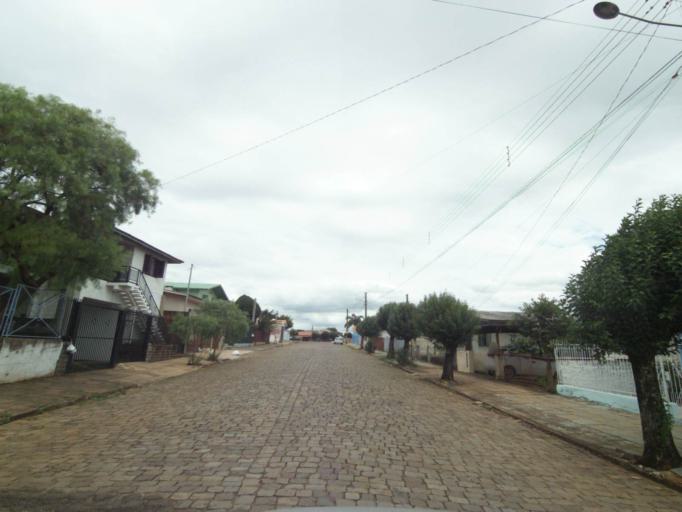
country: BR
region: Rio Grande do Sul
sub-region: Lagoa Vermelha
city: Lagoa Vermelha
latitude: -28.2126
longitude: -51.5357
